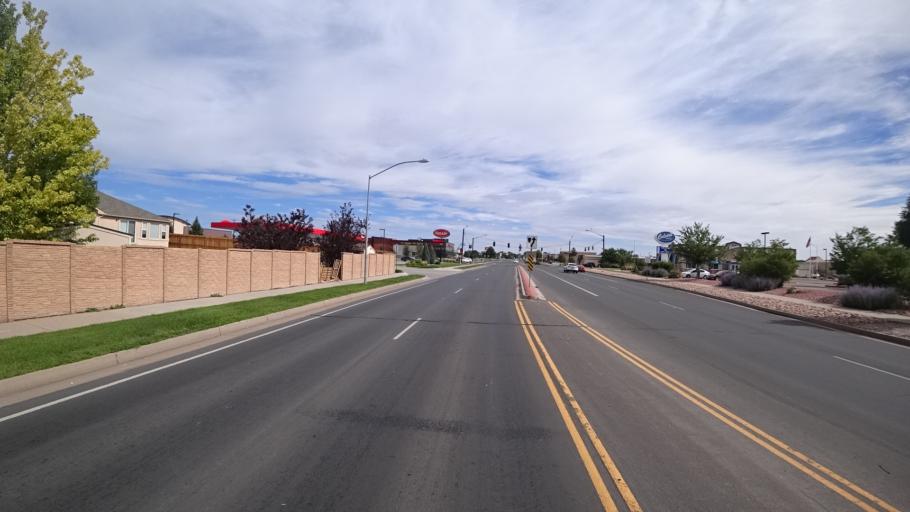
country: US
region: Colorado
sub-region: El Paso County
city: Fountain
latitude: 38.7147
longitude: -104.7015
